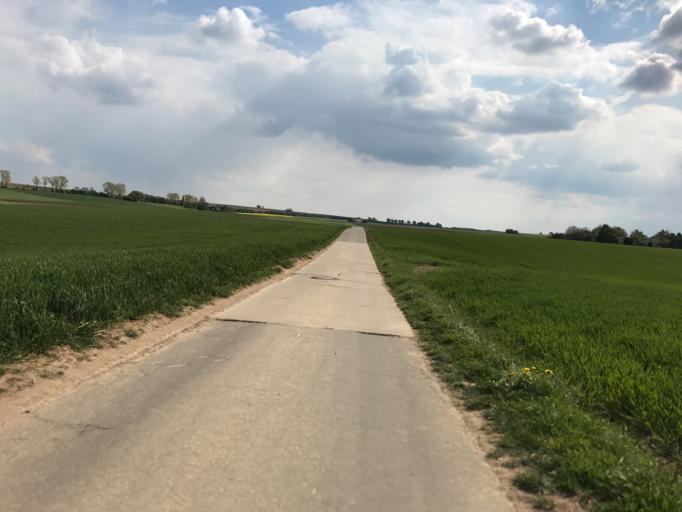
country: DE
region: Rheinland-Pfalz
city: Gau-Bischofsheim
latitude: 49.9468
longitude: 8.2742
